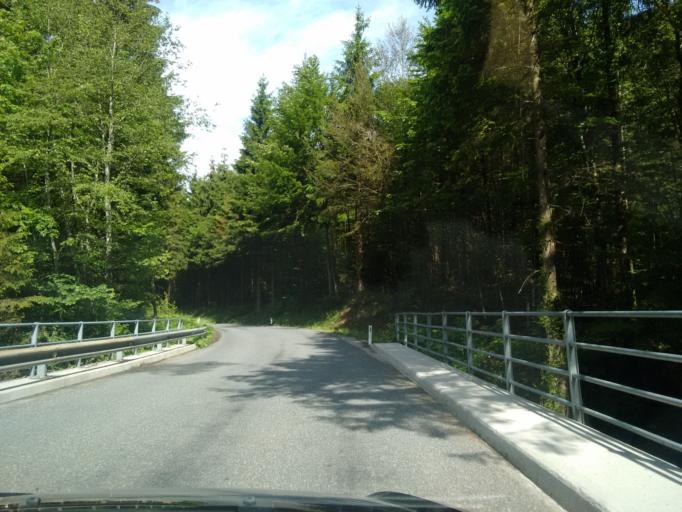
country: AT
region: Upper Austria
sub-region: Politischer Bezirk Gmunden
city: Ebensee
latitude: 47.8363
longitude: 13.7254
